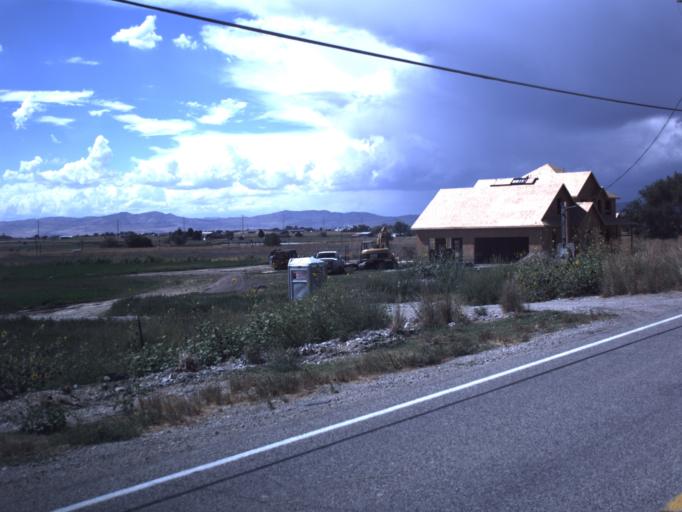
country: US
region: Utah
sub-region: Box Elder County
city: Honeyville
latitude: 41.6269
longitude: -112.0750
